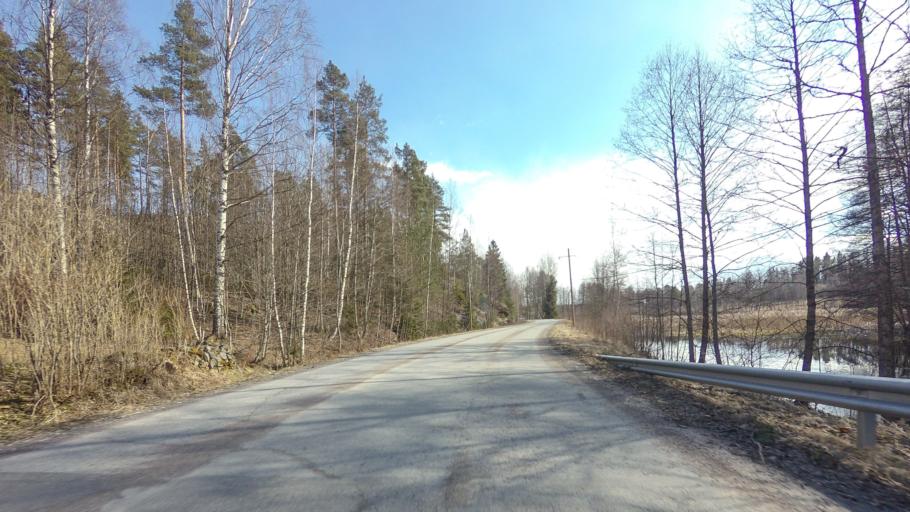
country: FI
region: Uusimaa
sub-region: Helsinki
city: Karjalohja
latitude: 60.2759
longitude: 23.6619
